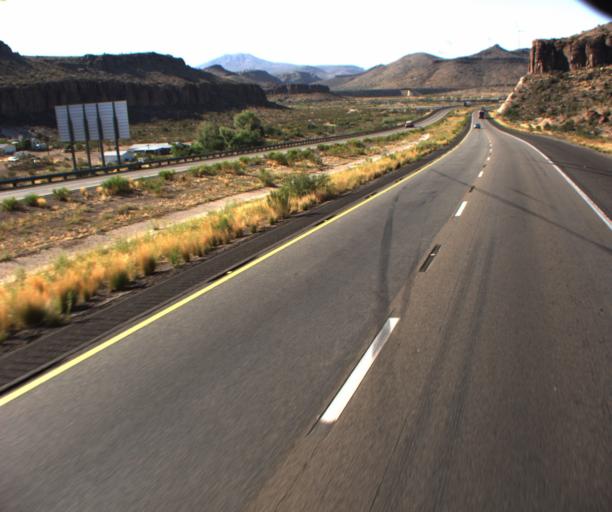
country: US
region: Arizona
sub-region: Mohave County
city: Kingman
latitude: 35.1709
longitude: -114.0754
